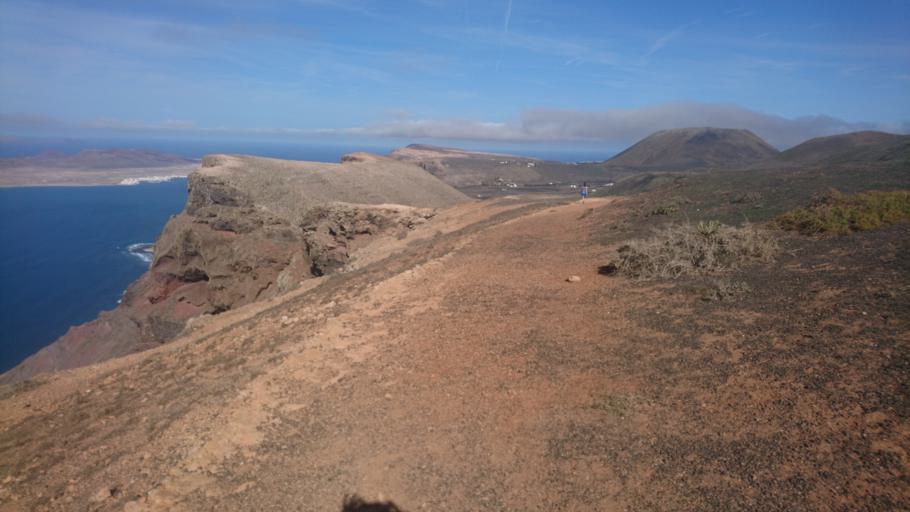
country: ES
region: Canary Islands
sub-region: Provincia de Las Palmas
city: Haria
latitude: 29.1691
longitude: -13.5130
